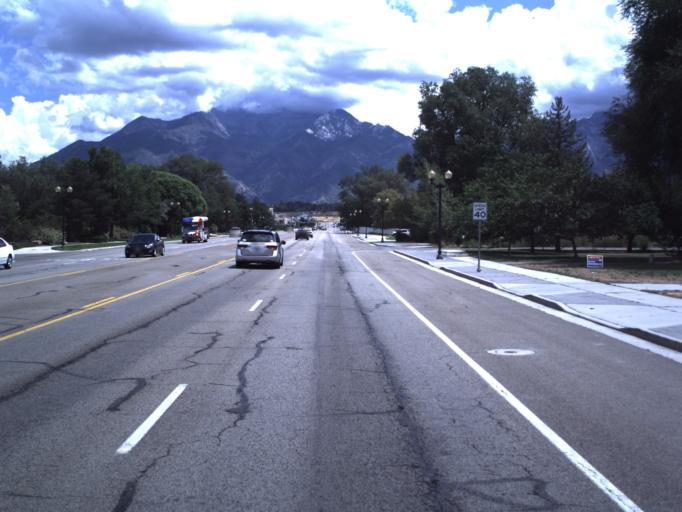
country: US
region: Utah
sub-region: Salt Lake County
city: Sandy City
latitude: 40.5881
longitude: -111.8809
